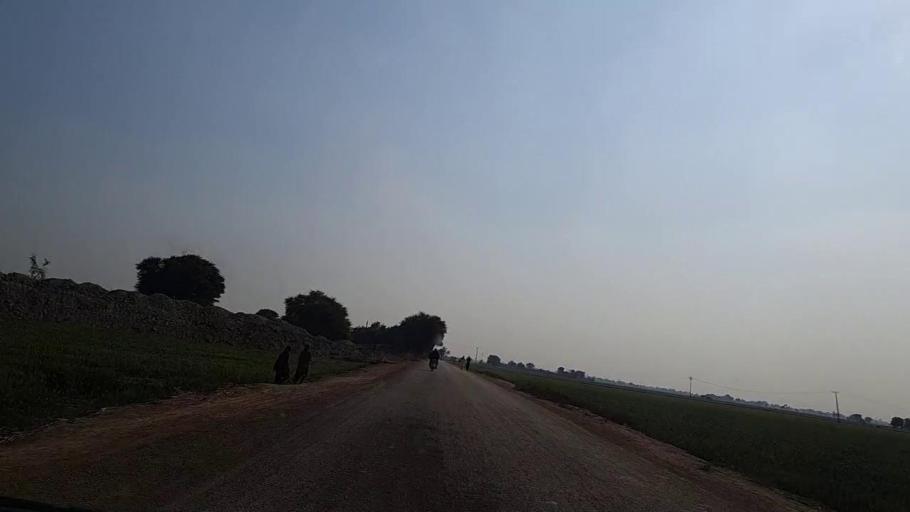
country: PK
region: Sindh
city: Sakrand
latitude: 26.1003
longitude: 68.2906
